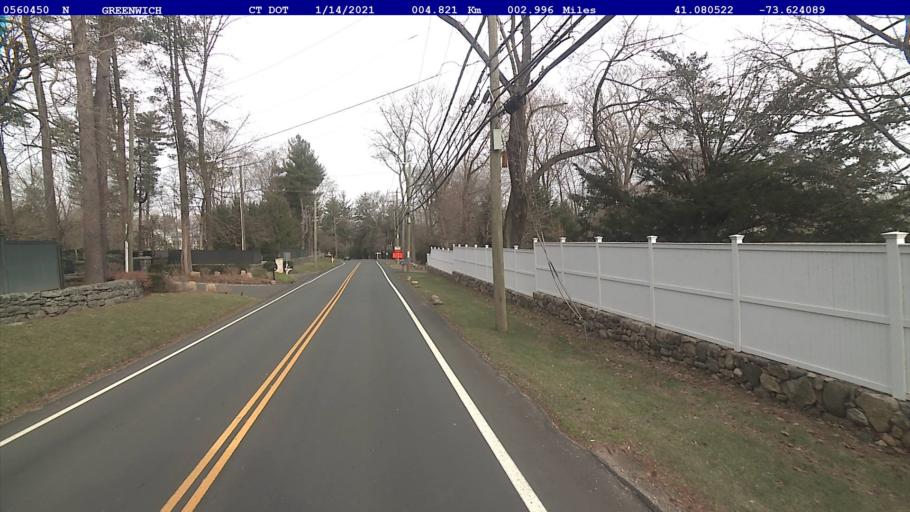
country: US
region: Connecticut
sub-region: Fairfield County
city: Cos Cob
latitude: 41.0805
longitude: -73.6241
